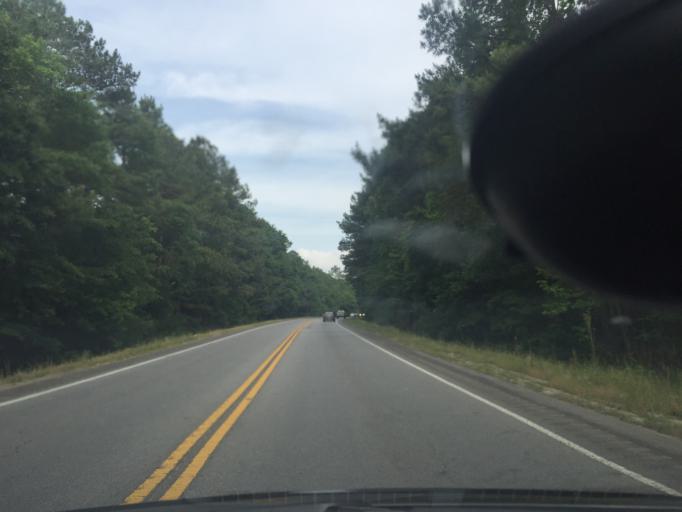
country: US
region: Georgia
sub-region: Bryan County
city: Richmond Hill
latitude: 32.0161
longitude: -81.3037
